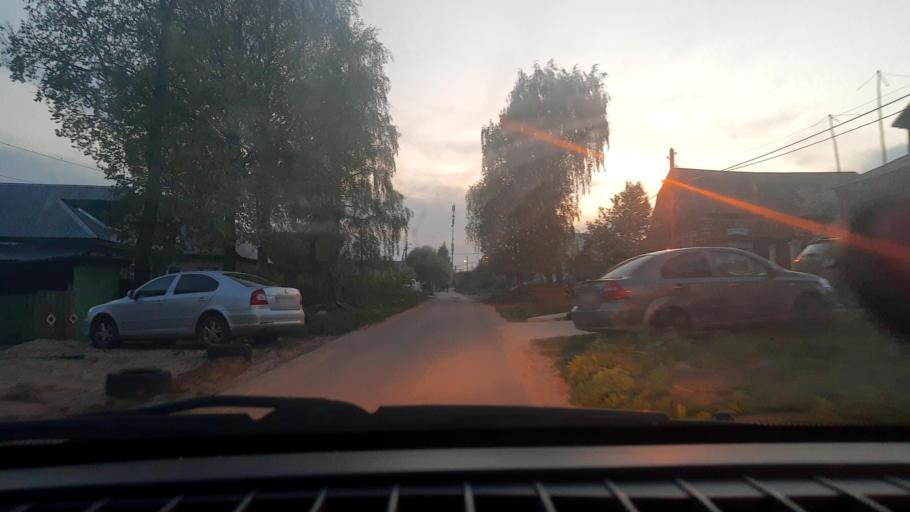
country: RU
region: Nizjnij Novgorod
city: Afonino
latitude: 56.2444
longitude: 44.0431
